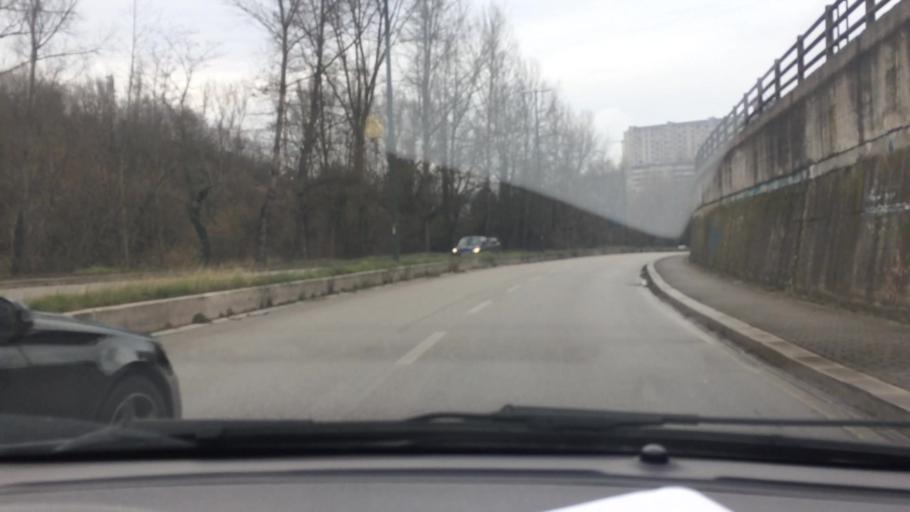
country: IT
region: Basilicate
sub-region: Provincia di Potenza
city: Potenza
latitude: 40.6350
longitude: 15.7953
